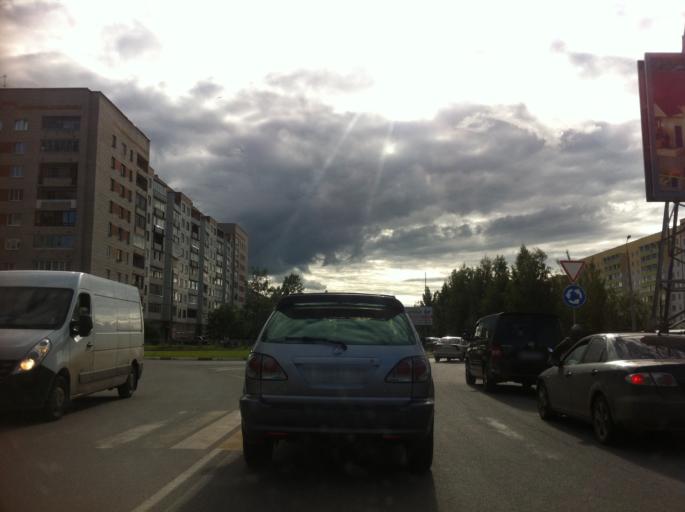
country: RU
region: Pskov
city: Pskov
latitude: 57.8226
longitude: 28.2884
